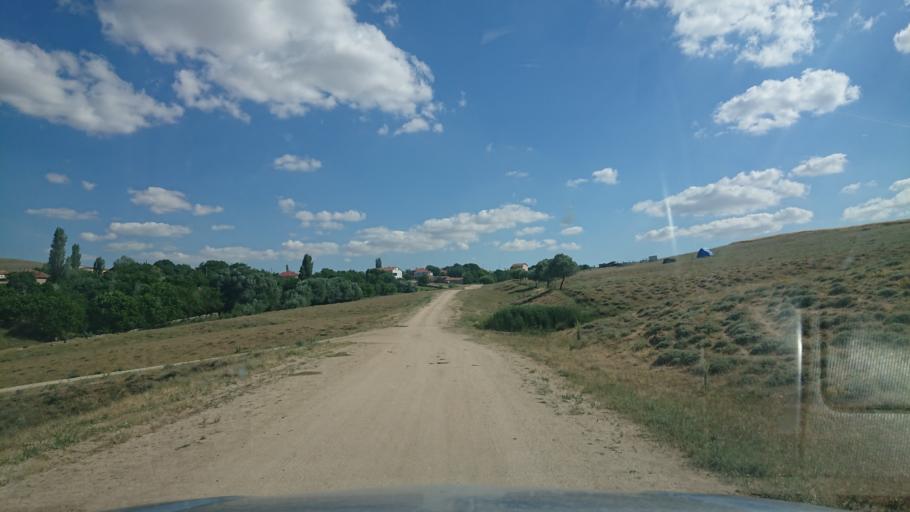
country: TR
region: Aksaray
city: Agacoren
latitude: 38.9076
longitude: 33.8562
